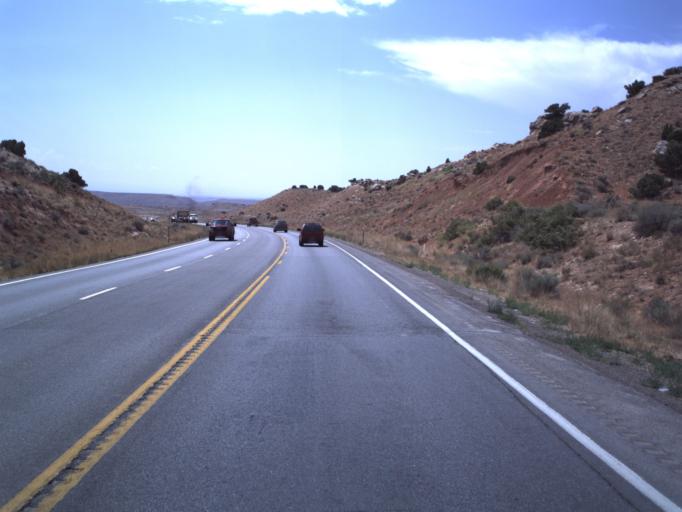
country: US
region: Utah
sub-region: Uintah County
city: Maeser
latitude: 40.4054
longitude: -109.5904
